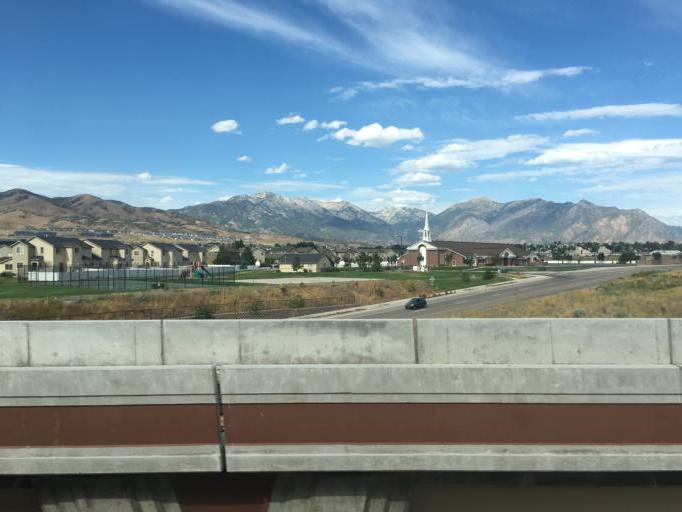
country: US
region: Utah
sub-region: Utah County
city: Lehi
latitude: 40.4128
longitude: -111.8823
